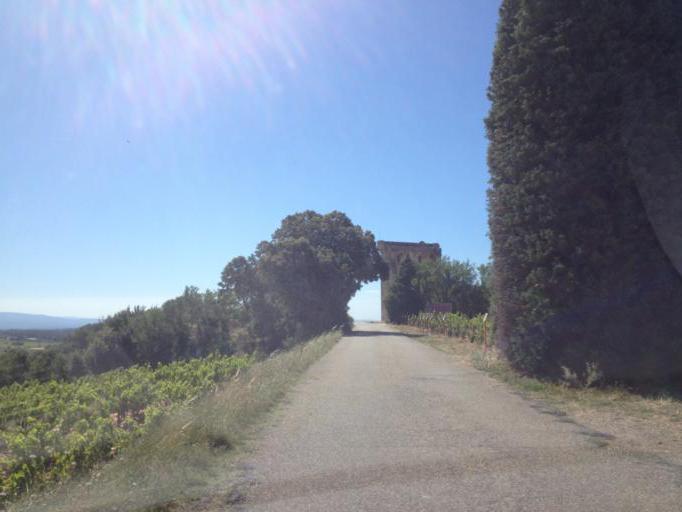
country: FR
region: Provence-Alpes-Cote d'Azur
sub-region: Departement du Vaucluse
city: Chateauneuf-du-Pape
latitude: 44.0591
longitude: 4.8282
